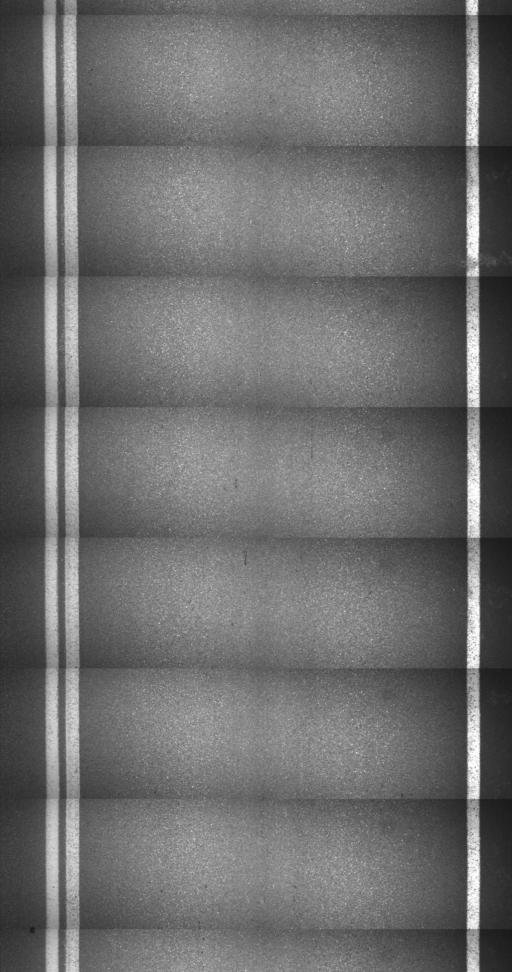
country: US
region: New Hampshire
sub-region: Grafton County
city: Woodsville
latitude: 44.1907
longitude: -72.0680
